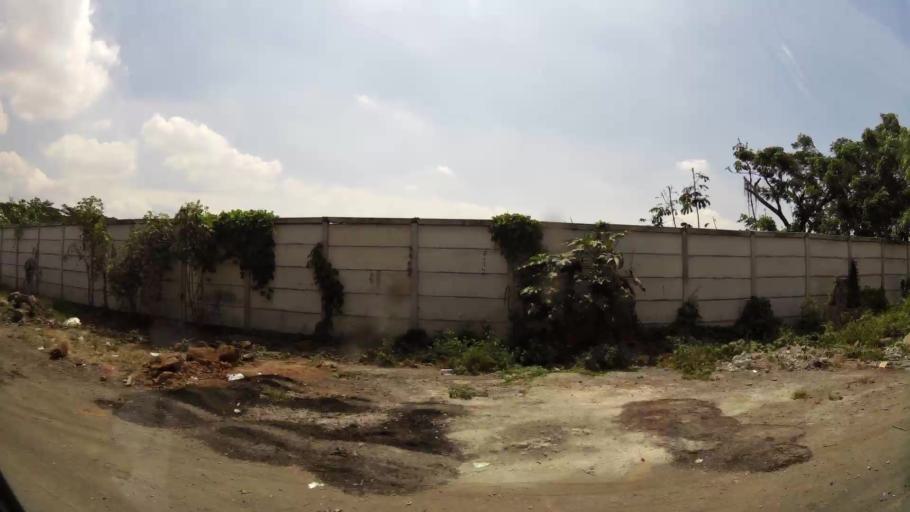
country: EC
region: Guayas
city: Eloy Alfaro
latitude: -2.1126
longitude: -79.9156
